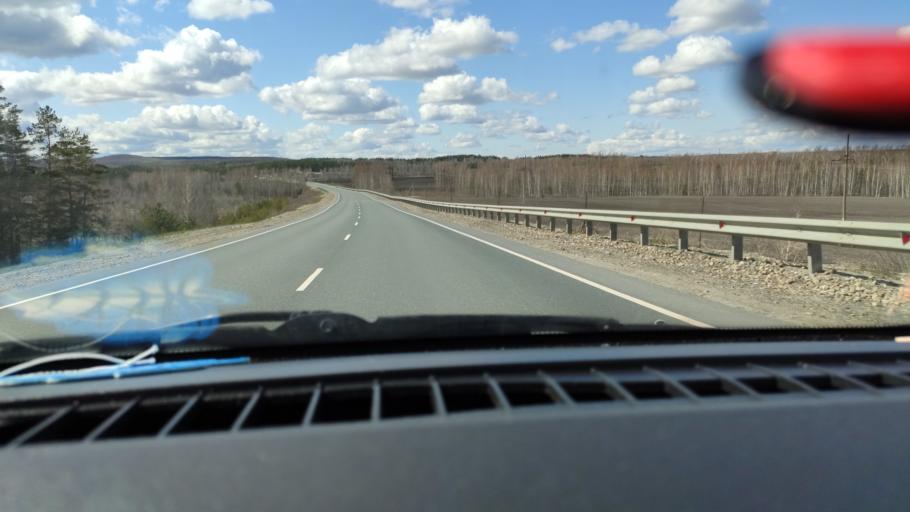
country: RU
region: Saratov
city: Khvalynsk
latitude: 52.5274
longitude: 48.0256
